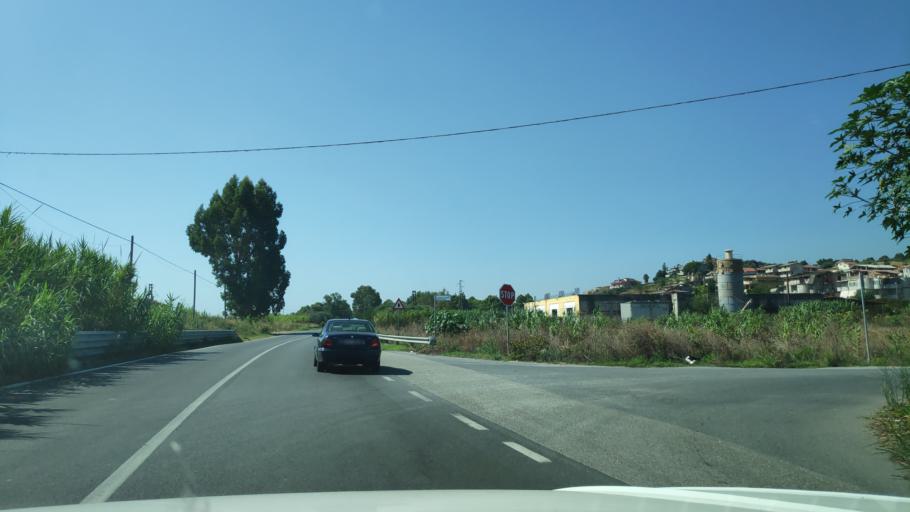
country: IT
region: Calabria
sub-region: Provincia di Reggio Calabria
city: Bovalino
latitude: 38.1250
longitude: 16.1595
